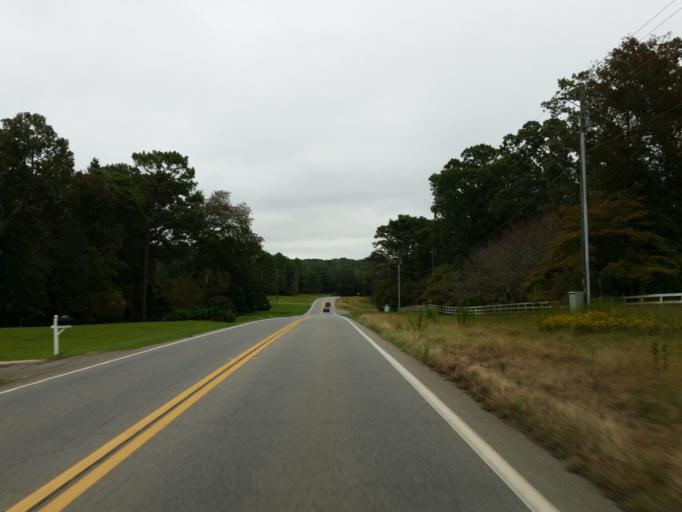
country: US
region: Georgia
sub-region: Houston County
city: Perry
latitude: 32.4858
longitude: -83.7903
